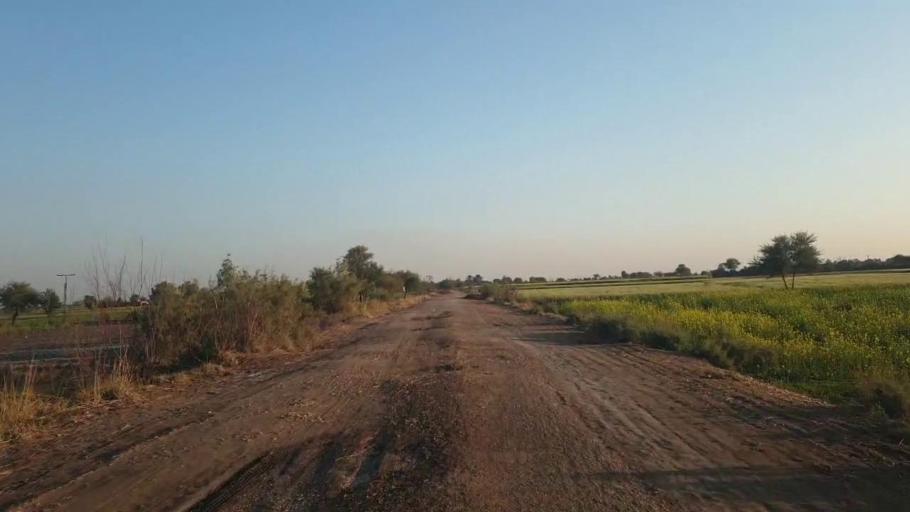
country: PK
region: Sindh
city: Khadro
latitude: 26.0768
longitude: 68.6885
